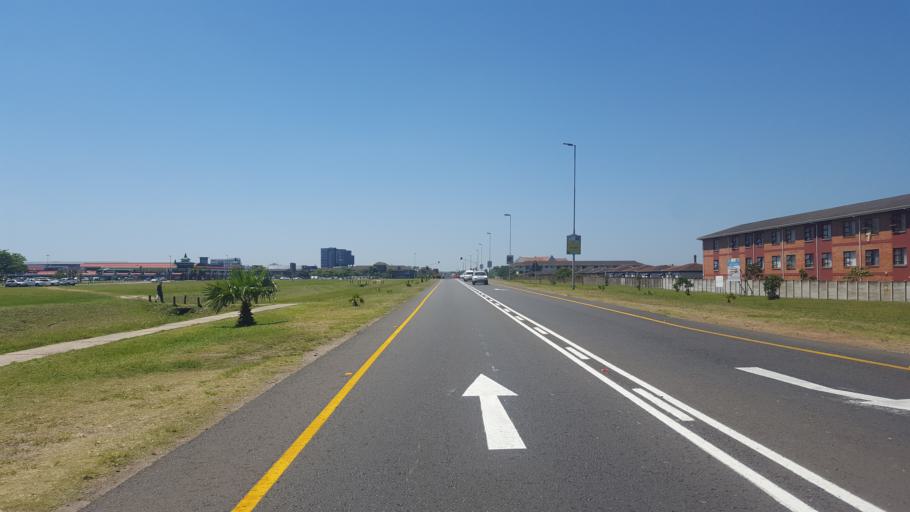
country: ZA
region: KwaZulu-Natal
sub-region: uThungulu District Municipality
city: Richards Bay
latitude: -28.7578
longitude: 32.0521
